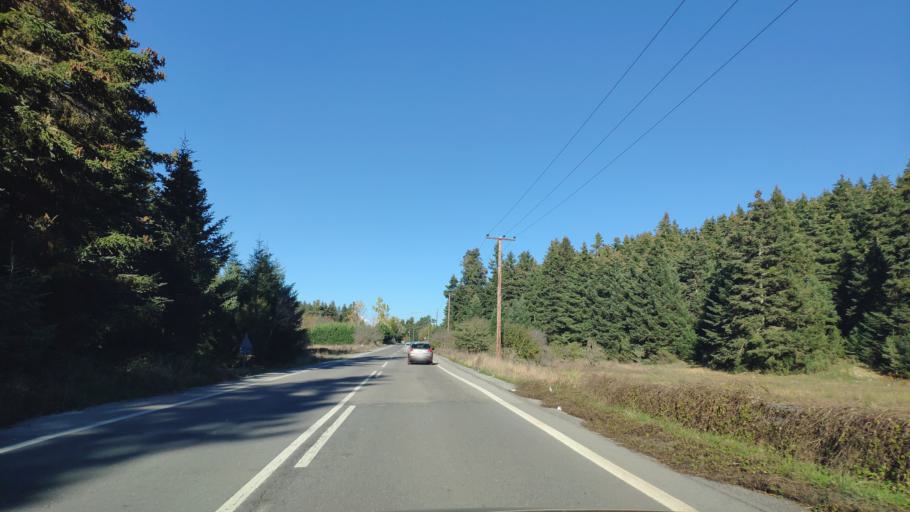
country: GR
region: Peloponnese
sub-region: Nomos Arkadias
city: Dimitsana
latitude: 37.6483
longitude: 22.1153
